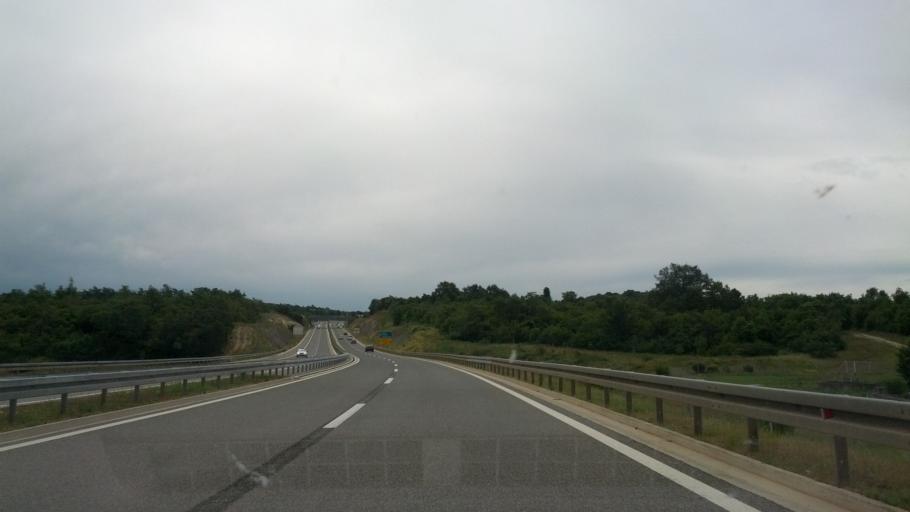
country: HR
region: Istarska
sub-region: Grad Rovinj
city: Rovinj
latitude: 45.1547
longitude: 13.7331
